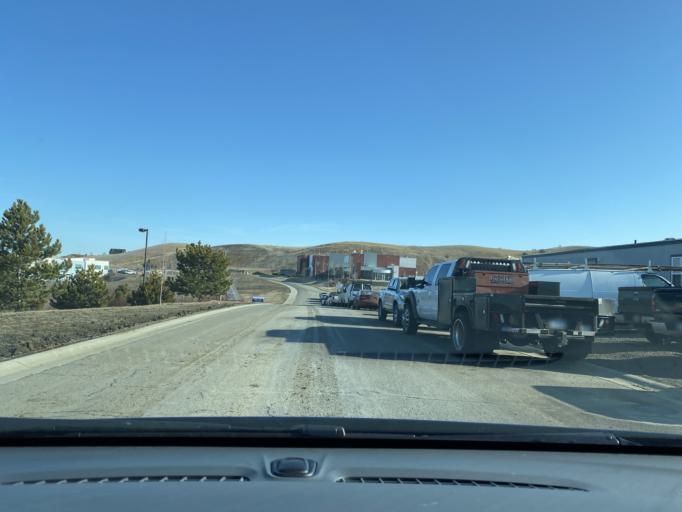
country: US
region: Washington
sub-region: Whitman County
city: Pullman
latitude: 46.7498
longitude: -117.1593
